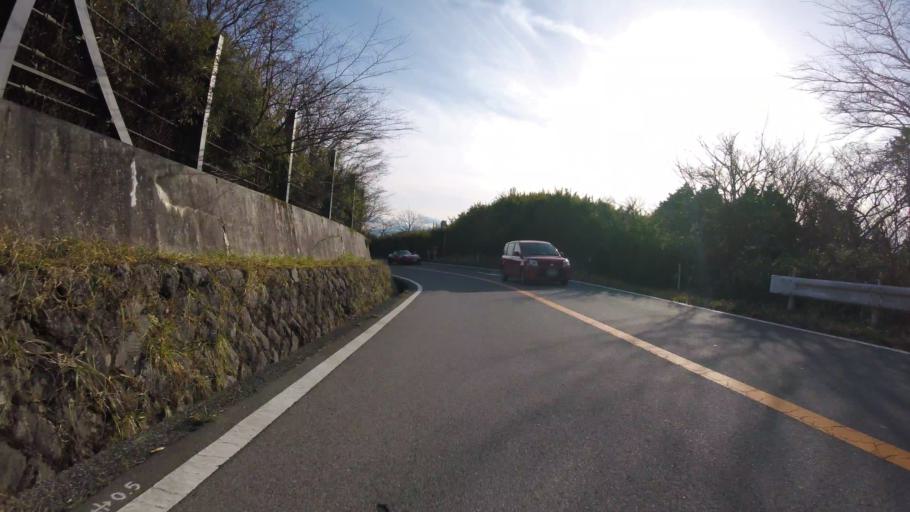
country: JP
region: Kanagawa
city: Yugawara
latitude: 35.1382
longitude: 139.0340
